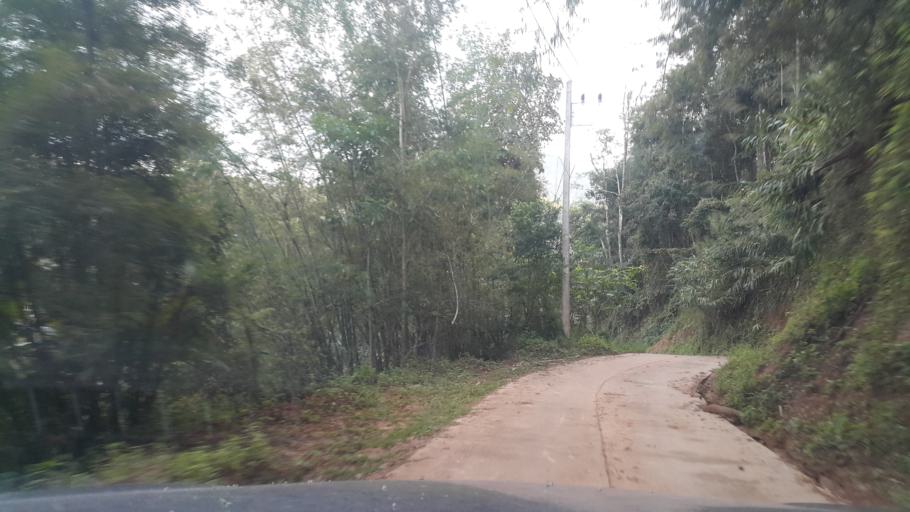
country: TH
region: Chiang Mai
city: Samoeng
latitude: 19.0096
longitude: 98.6680
